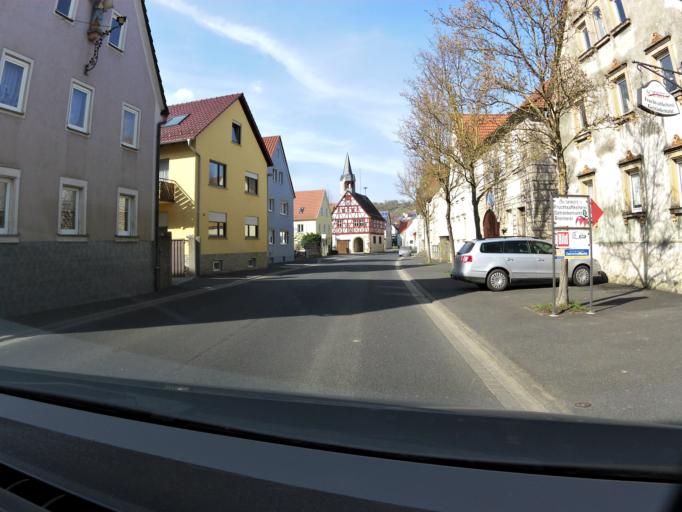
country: DE
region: Bavaria
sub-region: Regierungsbezirk Unterfranken
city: Bieberehren
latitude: 49.5148
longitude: 10.0080
